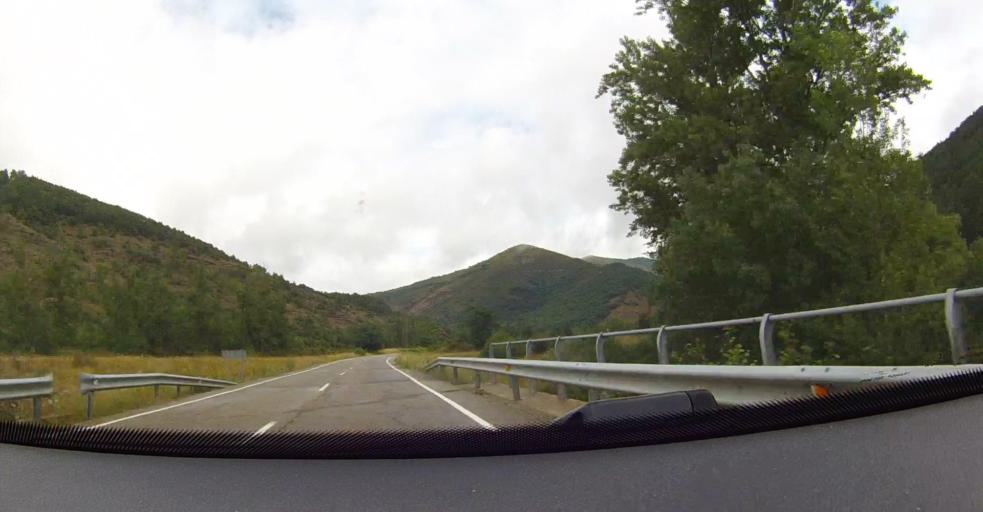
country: ES
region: Castille and Leon
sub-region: Provincia de Leon
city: Bonar
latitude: 42.8801
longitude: -5.3153
